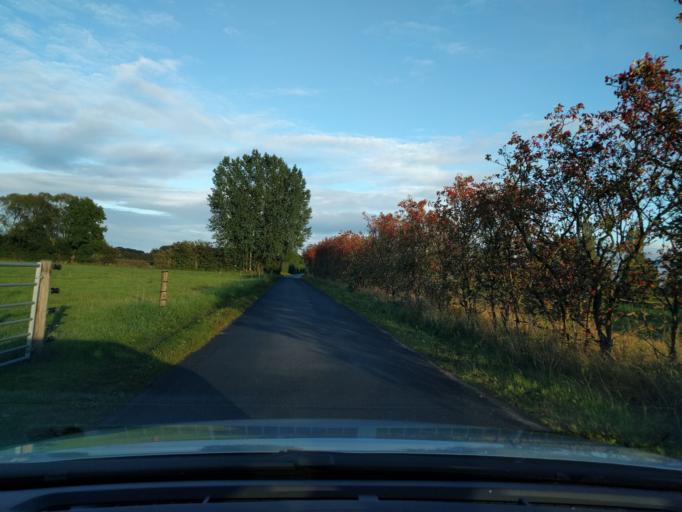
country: DK
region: South Denmark
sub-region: Odense Kommune
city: Bullerup
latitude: 55.4209
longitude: 10.5163
